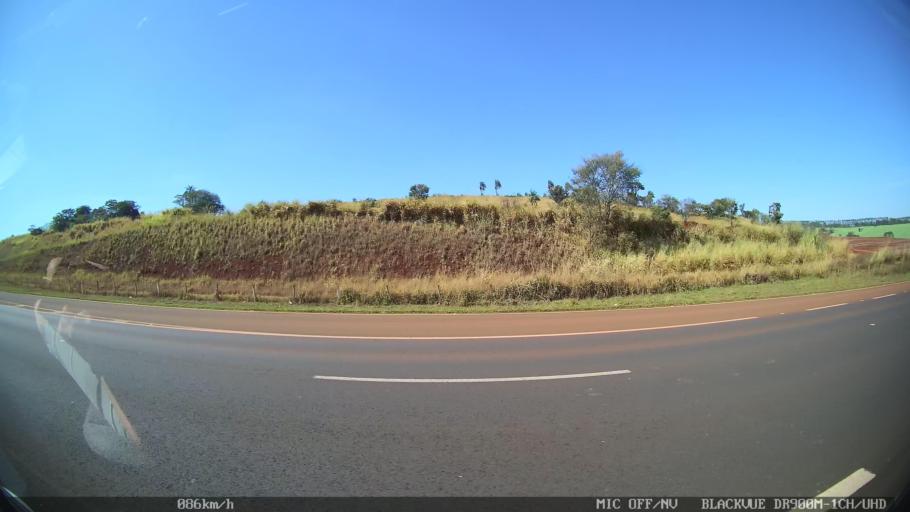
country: BR
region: Sao Paulo
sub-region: Franca
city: Franca
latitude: -20.6120
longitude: -47.4552
